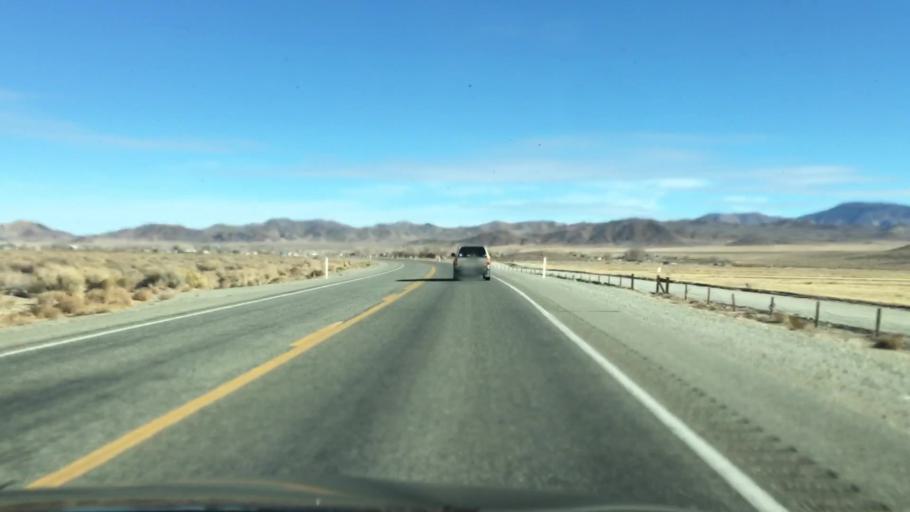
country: US
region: Nevada
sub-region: Lyon County
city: Yerington
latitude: 38.9976
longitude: -119.1071
